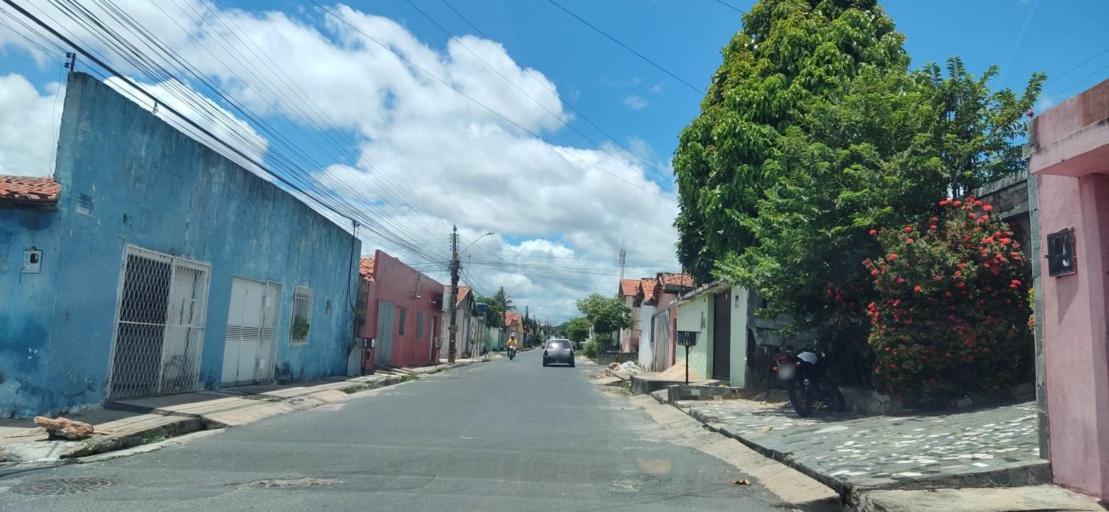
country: BR
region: Piaui
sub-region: Teresina
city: Teresina
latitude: -5.1531
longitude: -42.7858
